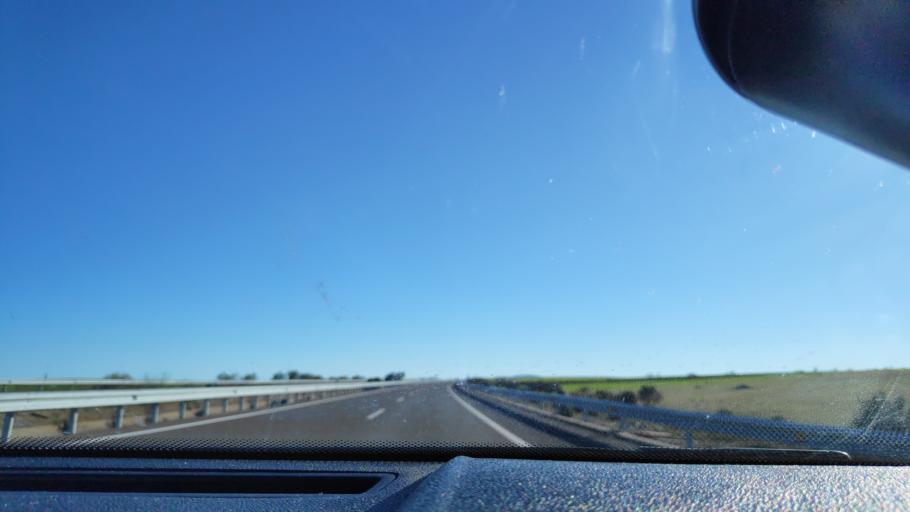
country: ES
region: Extremadura
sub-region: Provincia de Badajoz
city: Fuente de Cantos
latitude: 38.2100
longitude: -6.2871
